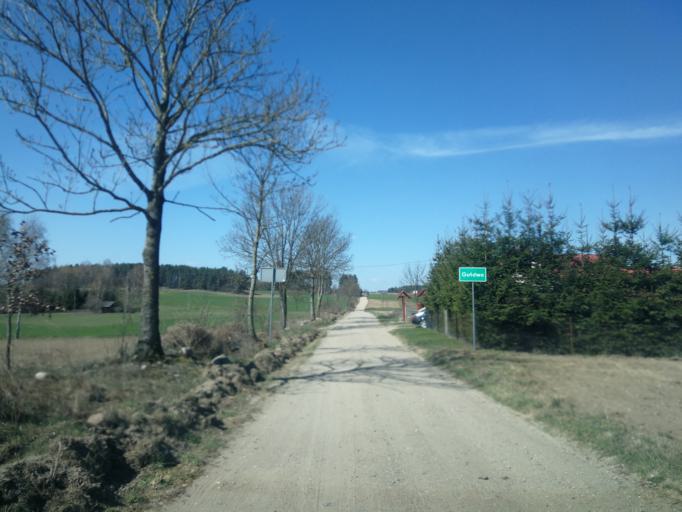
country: PL
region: Warmian-Masurian Voivodeship
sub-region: Powiat dzialdowski
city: Rybno
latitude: 53.4392
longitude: 19.9453
